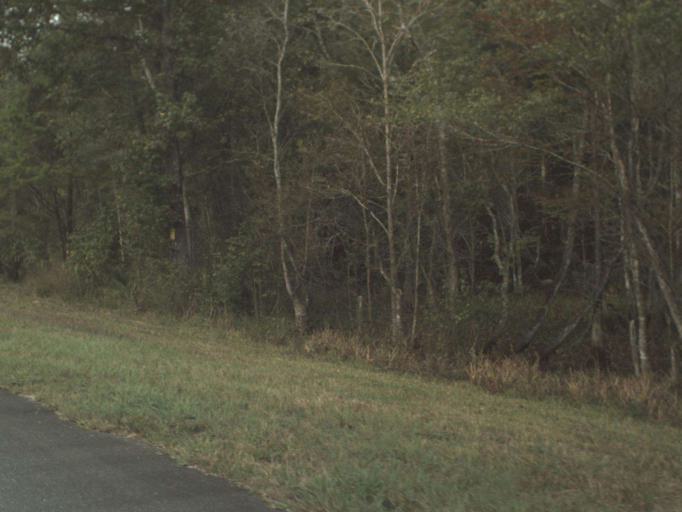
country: US
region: Florida
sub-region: Leon County
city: Woodville
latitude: 30.1608
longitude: -84.0019
